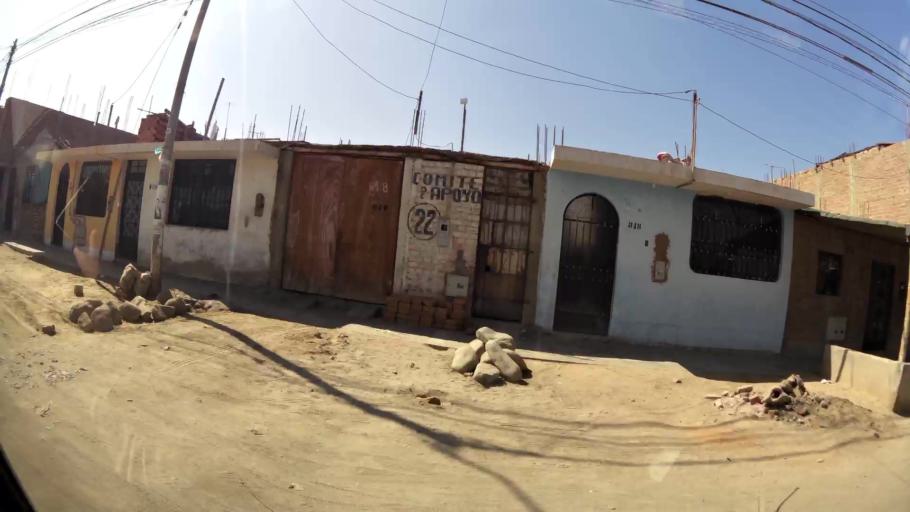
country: PE
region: Ica
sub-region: Provincia de Ica
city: La Tinguina
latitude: -14.0327
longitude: -75.7097
